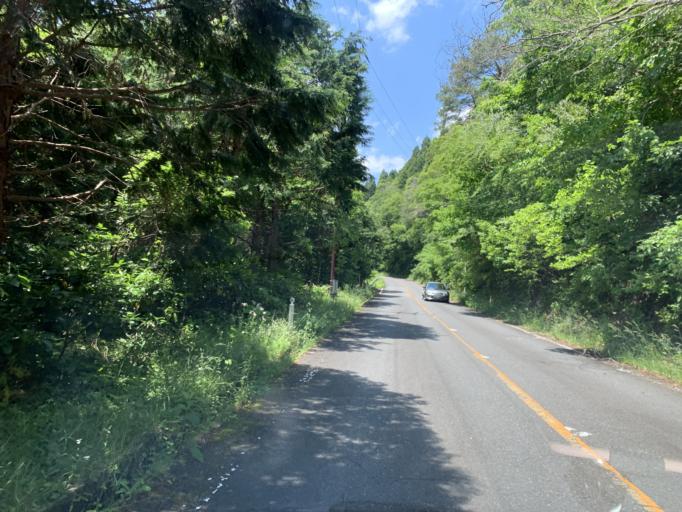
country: JP
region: Miyagi
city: Matsushima
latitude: 38.3629
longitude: 141.0504
